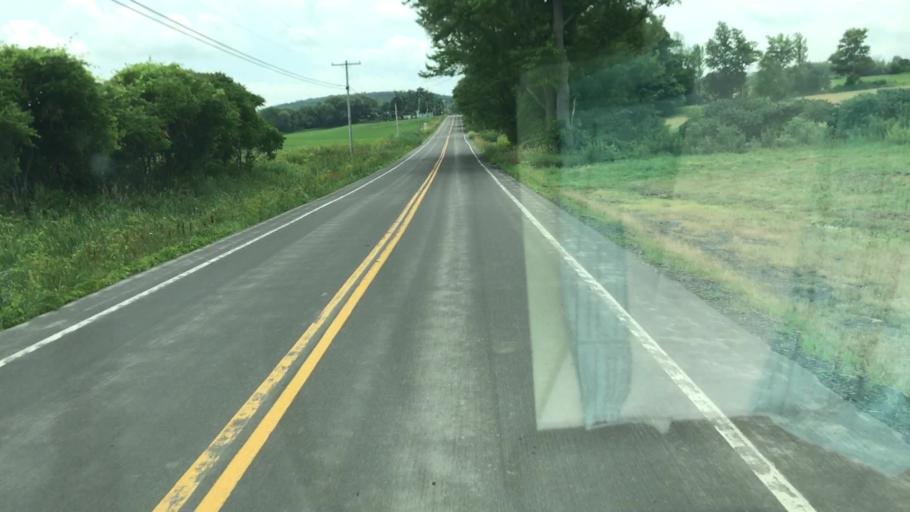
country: US
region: New York
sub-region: Onondaga County
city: Manlius
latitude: 42.9293
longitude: -75.9764
